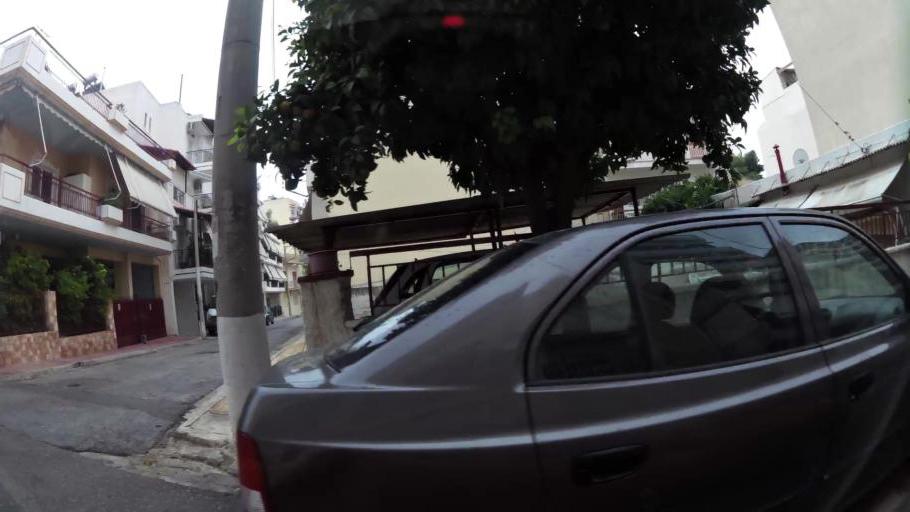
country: GR
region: Attica
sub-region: Nomarchia Athinas
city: Ilion
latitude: 38.0234
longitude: 23.7074
